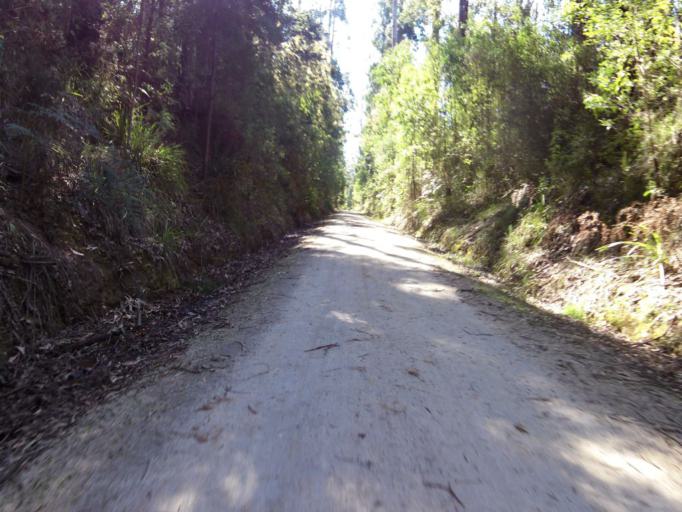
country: AU
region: Victoria
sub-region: Latrobe
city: Moe
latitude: -38.3823
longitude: 146.2432
